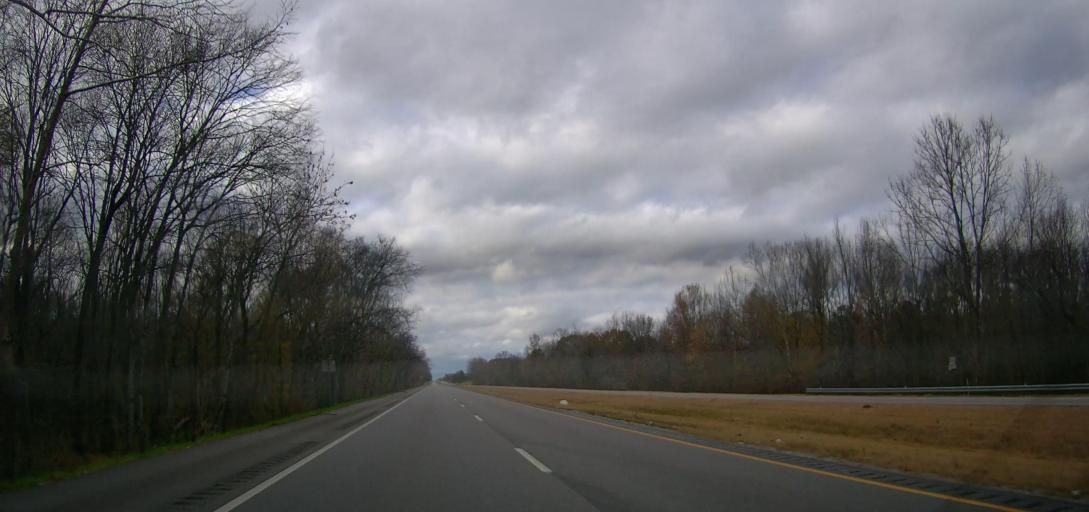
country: US
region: Alabama
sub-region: Lawrence County
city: Town Creek
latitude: 34.6346
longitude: -87.4925
